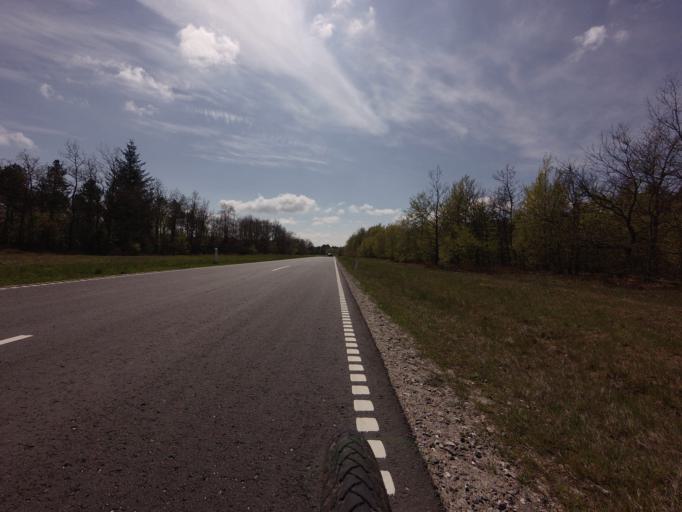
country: DK
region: North Denmark
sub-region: Jammerbugt Kommune
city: Brovst
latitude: 57.1658
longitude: 9.5756
